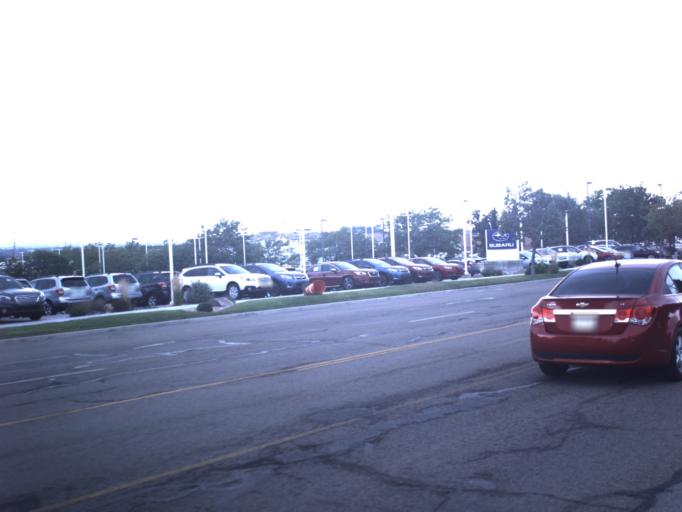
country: US
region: Utah
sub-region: Salt Lake County
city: White City
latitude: 40.5531
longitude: -111.8907
